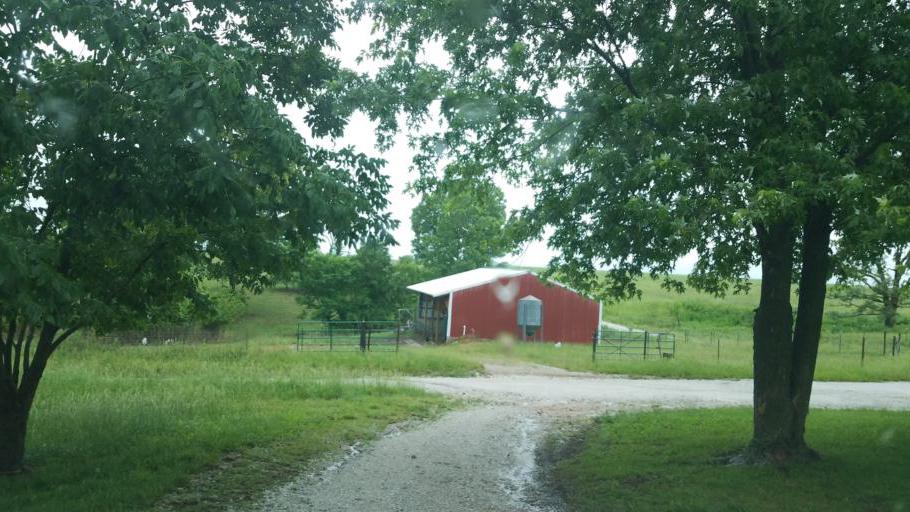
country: US
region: Missouri
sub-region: Moniteau County
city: California
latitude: 38.7597
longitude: -92.6059
